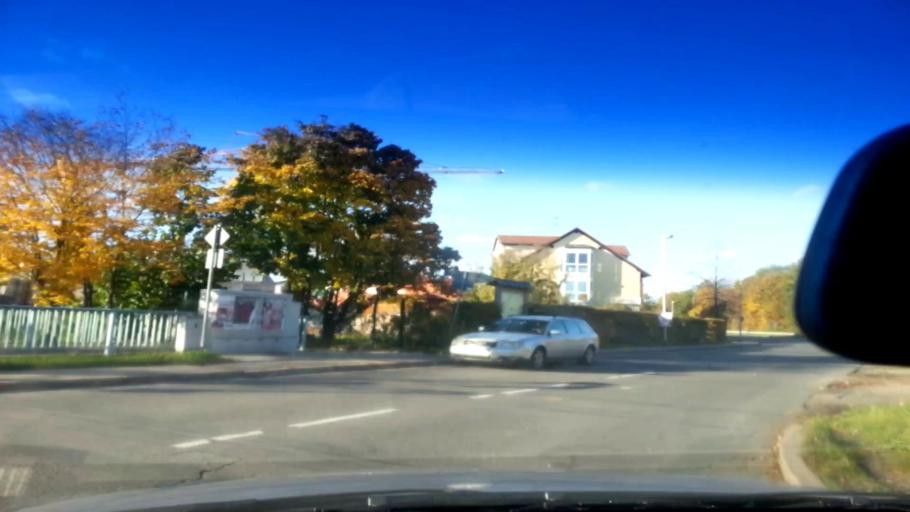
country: DE
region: Bavaria
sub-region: Upper Franconia
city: Rattelsdorf
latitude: 50.0139
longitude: 10.8908
